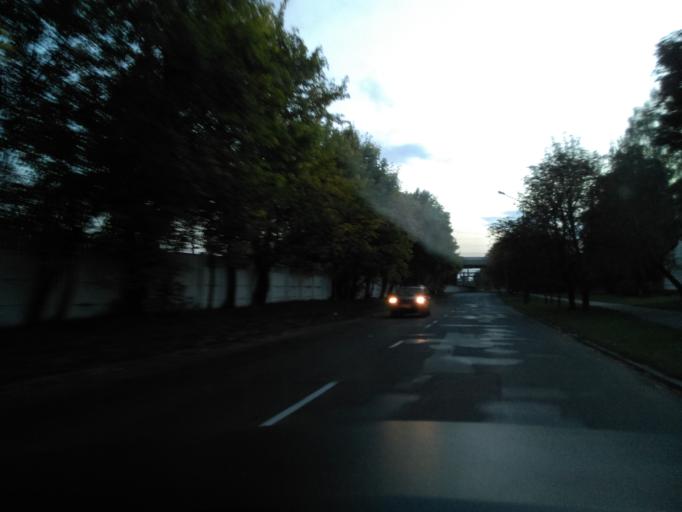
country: BY
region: Minsk
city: Minsk
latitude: 53.9050
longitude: 27.6375
